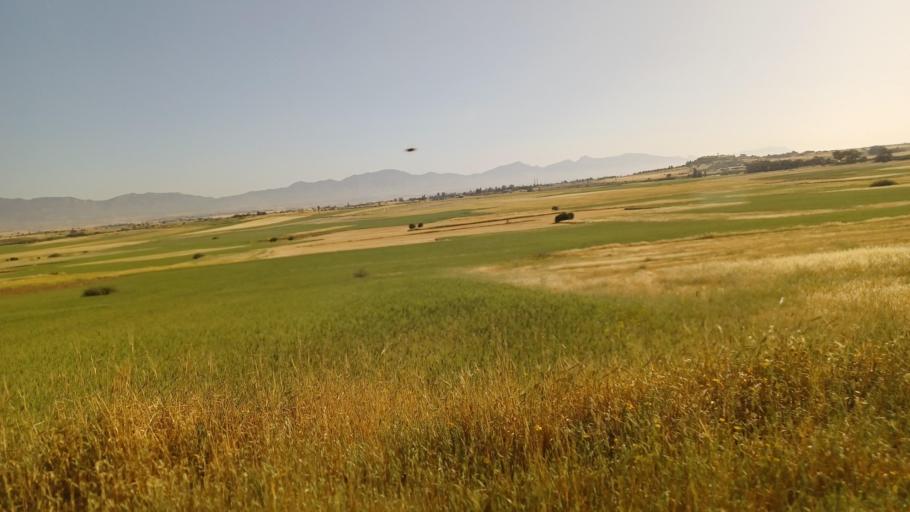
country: CY
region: Lefkosia
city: Mammari
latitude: 35.1648
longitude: 33.2369
